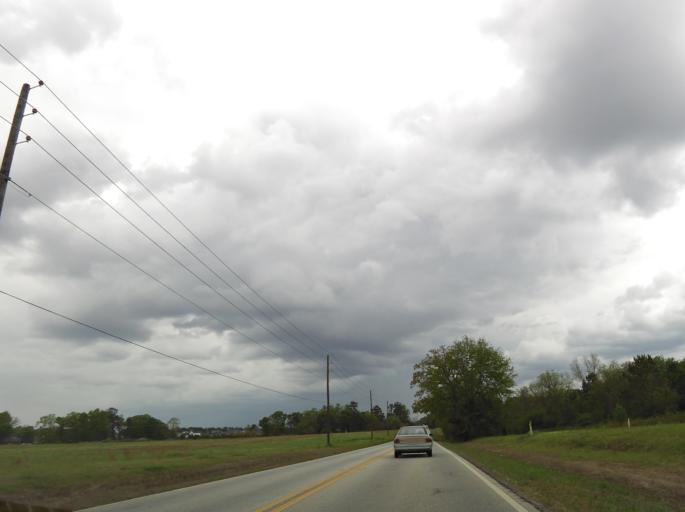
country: US
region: Georgia
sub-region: Houston County
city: Robins Air Force Base
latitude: 32.5606
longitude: -83.5867
